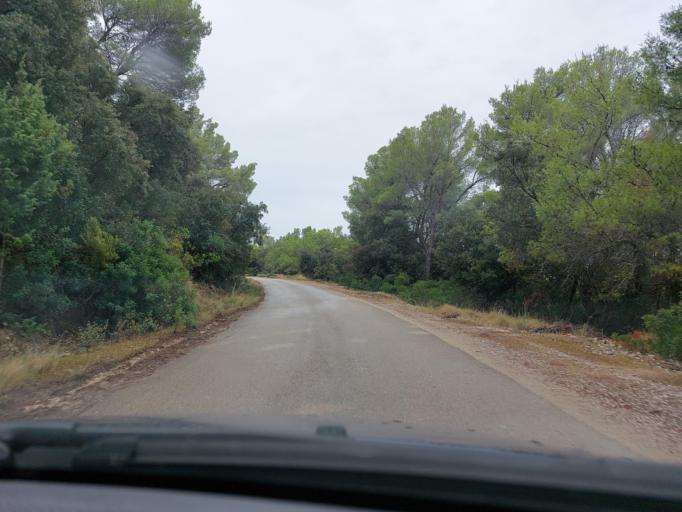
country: HR
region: Dubrovacko-Neretvanska
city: Smokvica
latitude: 42.7440
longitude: 16.8317
